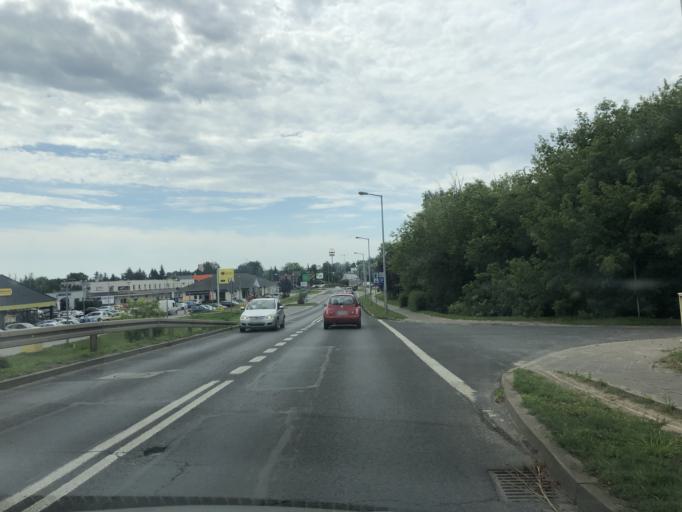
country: PL
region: Greater Poland Voivodeship
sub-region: Powiat poznanski
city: Lubon
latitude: 52.3539
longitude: 16.8832
